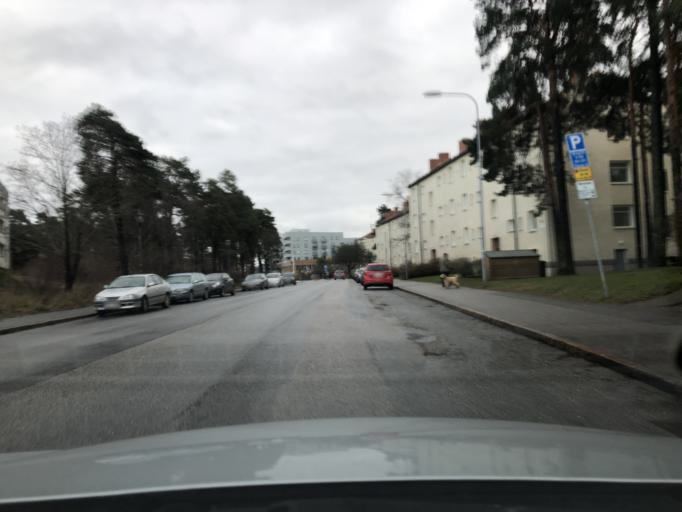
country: SE
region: Stockholm
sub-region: Stockholms Kommun
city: Arsta
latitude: 59.2991
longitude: 18.0586
